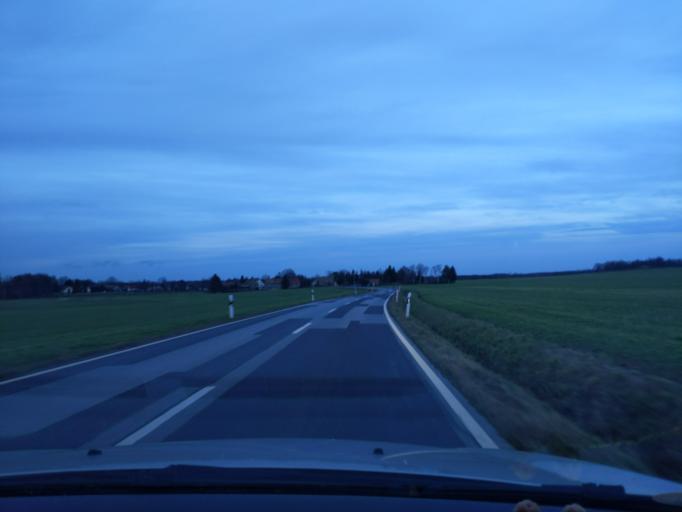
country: DE
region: Saxony
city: Malschwitz
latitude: 51.2211
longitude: 14.4999
